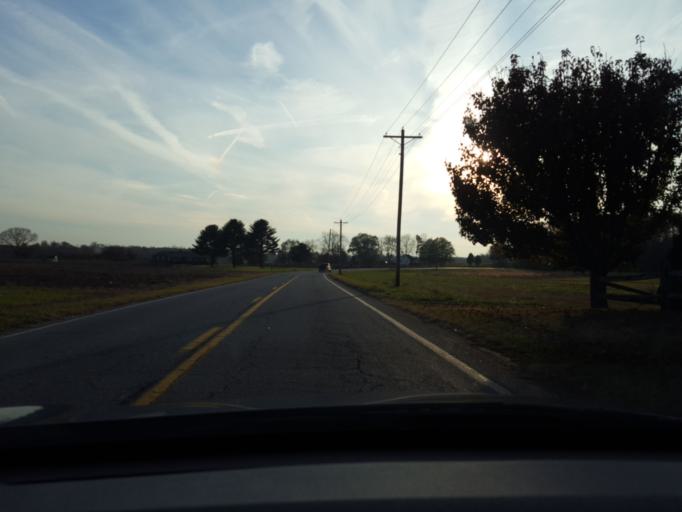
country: US
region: Maryland
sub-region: Charles County
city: Hughesville
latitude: 38.5303
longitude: -76.8195
